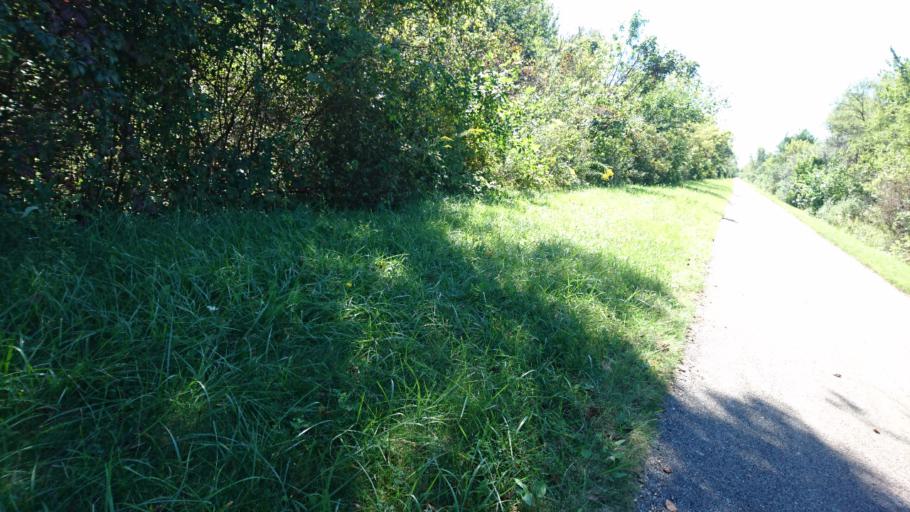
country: US
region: Illinois
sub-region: Cook County
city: Lansing
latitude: 41.5921
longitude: -87.5494
